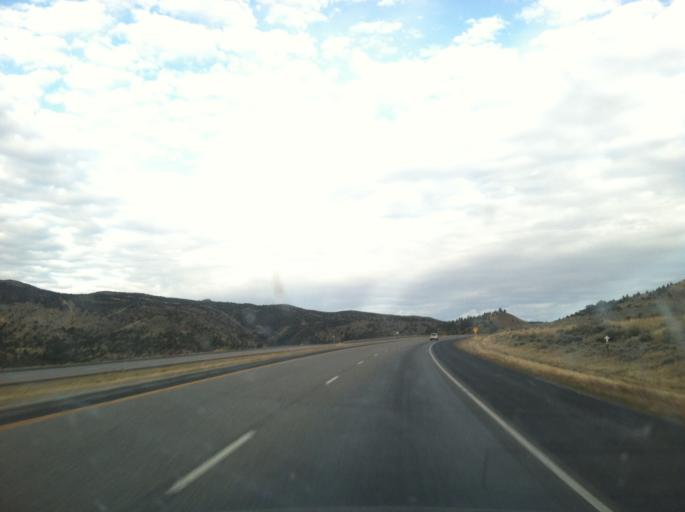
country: US
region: Montana
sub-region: Jefferson County
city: Whitehall
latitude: 45.8827
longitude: -111.9110
